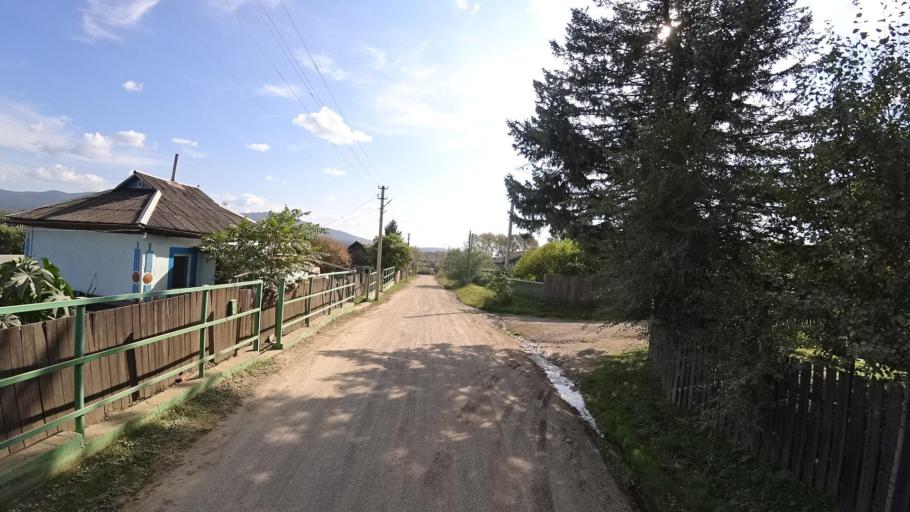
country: RU
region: Jewish Autonomous Oblast
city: Birakan
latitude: 48.9963
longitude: 131.7248
